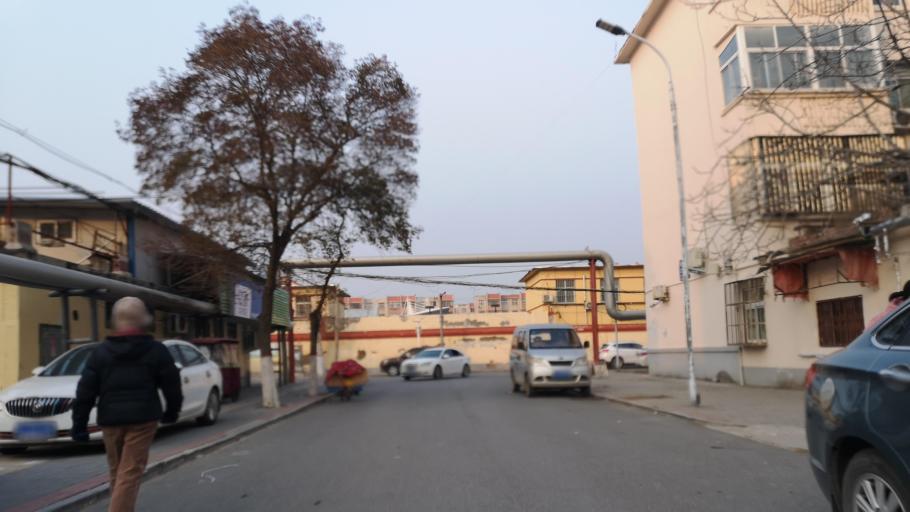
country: CN
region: Henan Sheng
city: Zhongyuanlu
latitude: 35.7684
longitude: 115.1008
